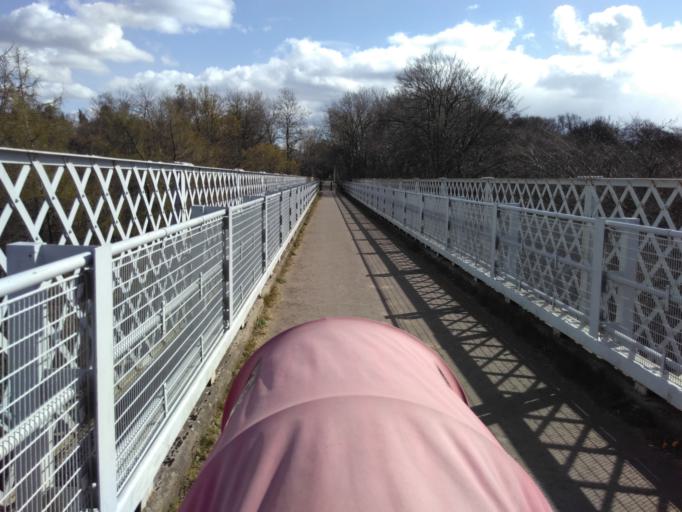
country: GB
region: Scotland
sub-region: Midlothian
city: Loanhead
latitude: 55.8718
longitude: -3.1510
